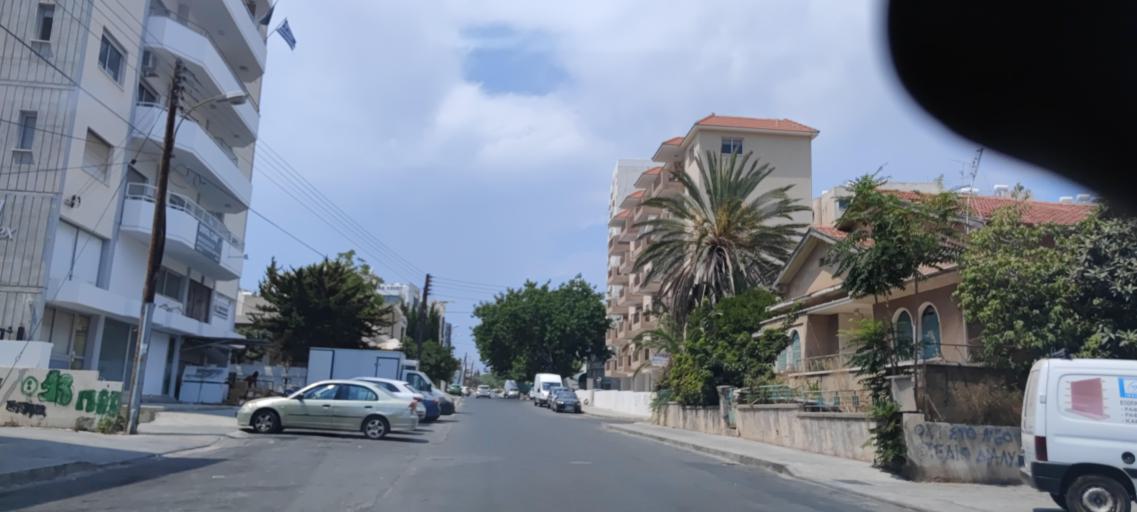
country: CY
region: Limassol
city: Limassol
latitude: 34.6835
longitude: 33.0404
